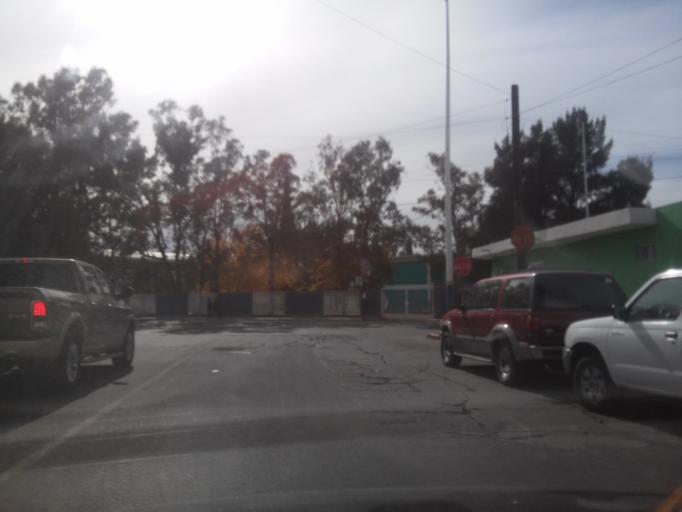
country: MX
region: Durango
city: Victoria de Durango
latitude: 24.0151
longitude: -104.6559
